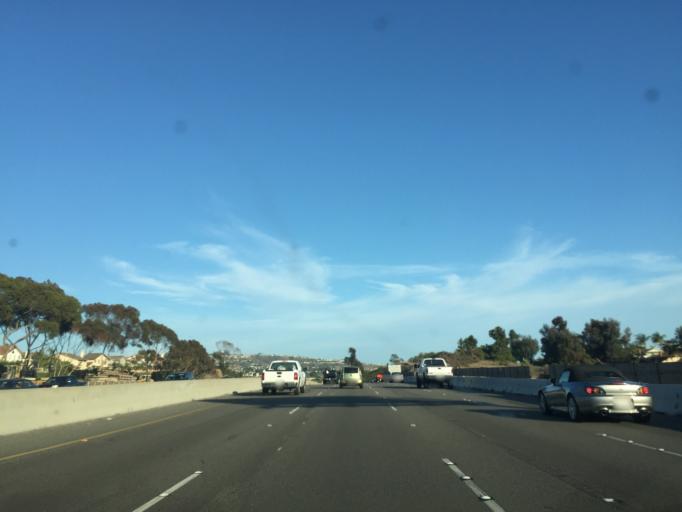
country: US
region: California
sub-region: Orange County
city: San Clemente
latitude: 33.4499
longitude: -117.6395
